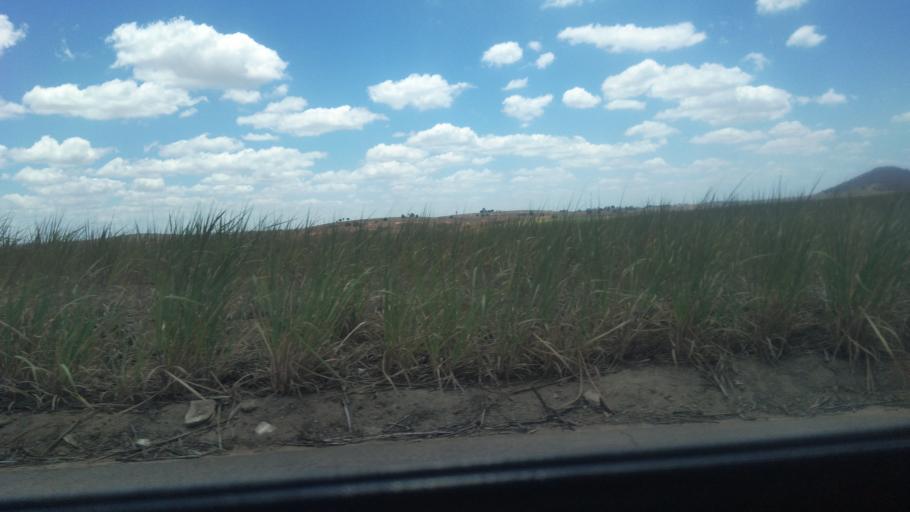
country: BR
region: Pernambuco
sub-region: Nazare Da Mata
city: Nazare da Mata
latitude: -7.7358
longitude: -35.2716
